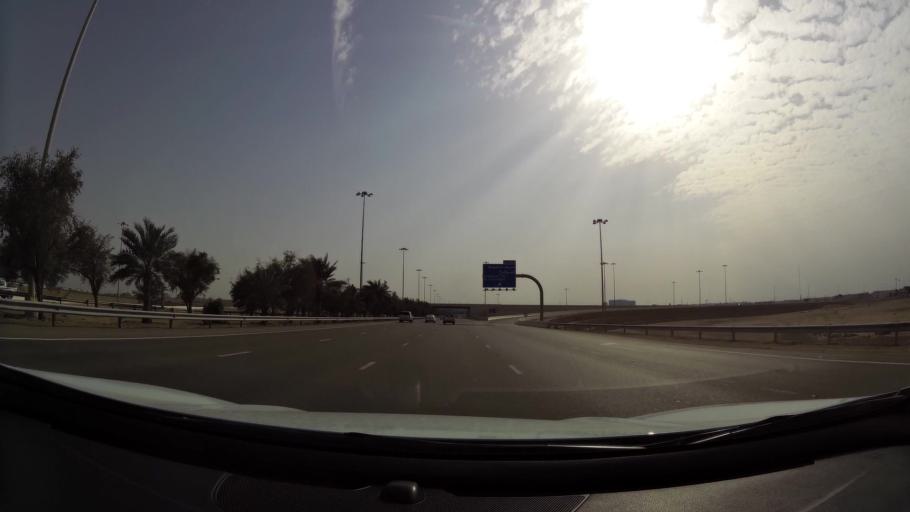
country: AE
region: Abu Dhabi
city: Abu Dhabi
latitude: 24.3425
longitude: 54.6380
